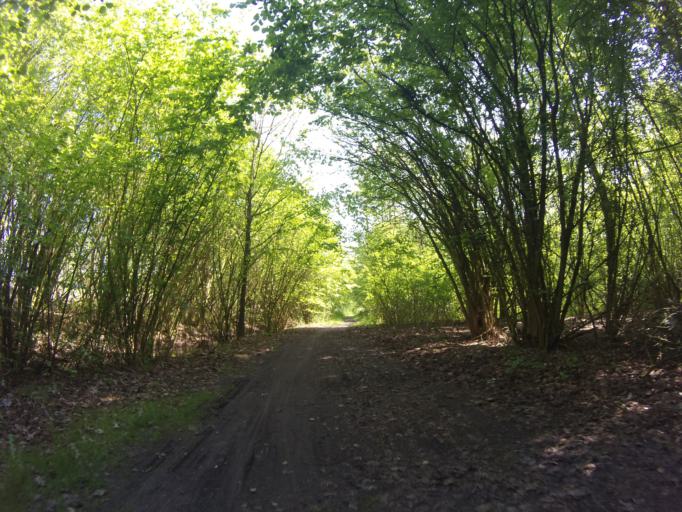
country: NL
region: Flevoland
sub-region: Gemeente Zeewolde
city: Zeewolde
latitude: 52.2942
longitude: 5.5343
